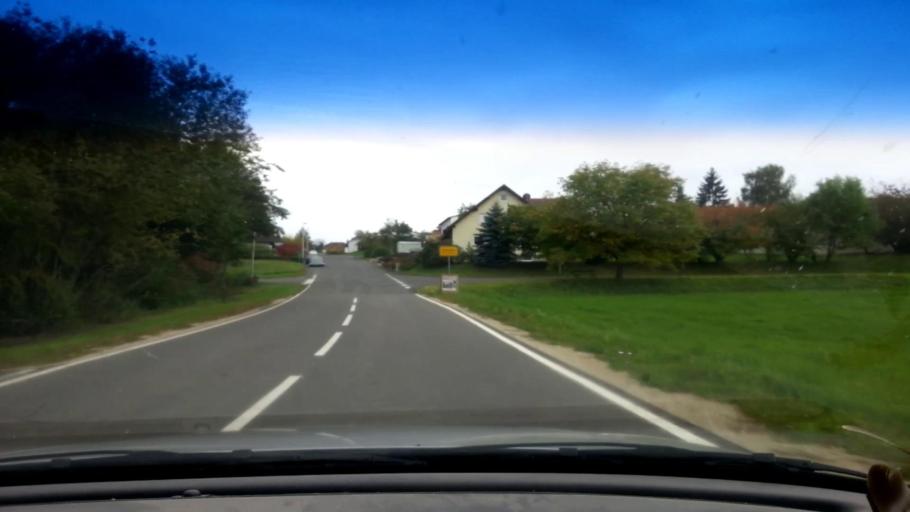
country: DE
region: Bavaria
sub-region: Upper Franconia
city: Gerach
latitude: 50.0331
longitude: 10.8106
